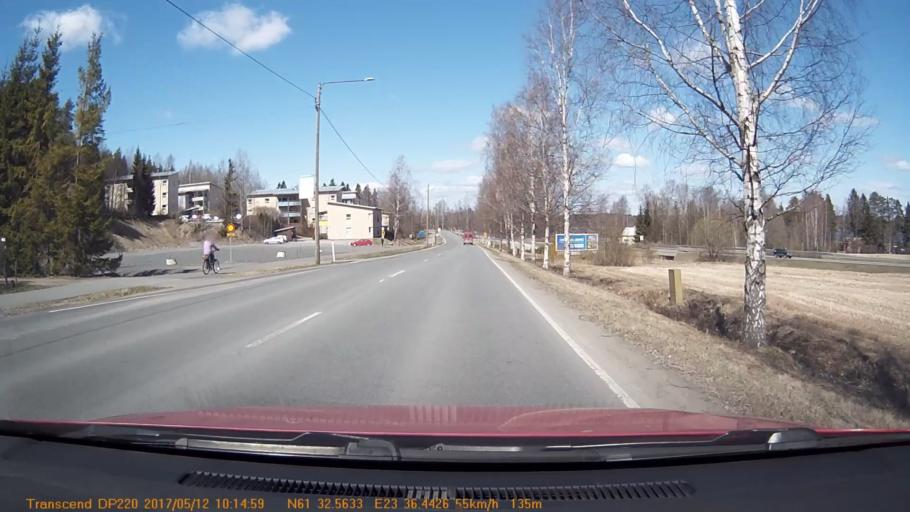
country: FI
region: Pirkanmaa
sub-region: Tampere
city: Yloejaervi
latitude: 61.5426
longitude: 23.6075
